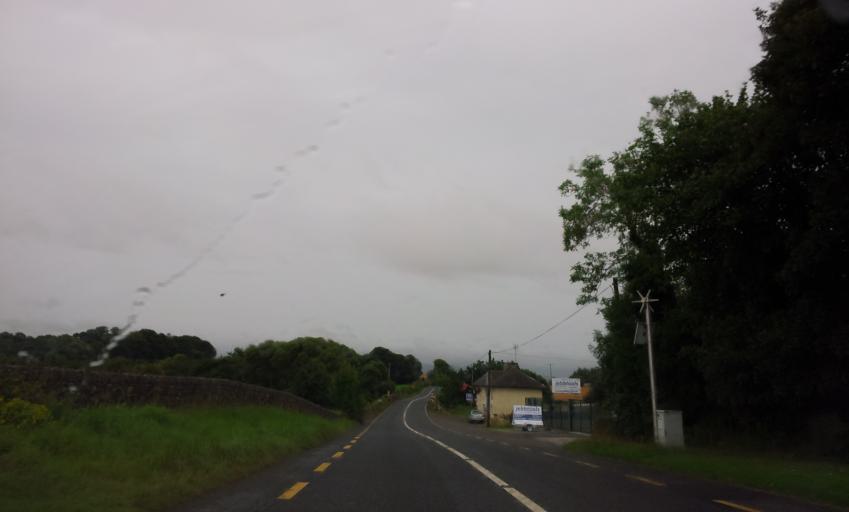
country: IE
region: Munster
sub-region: County Cork
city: Mallow
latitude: 52.2209
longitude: -8.5034
